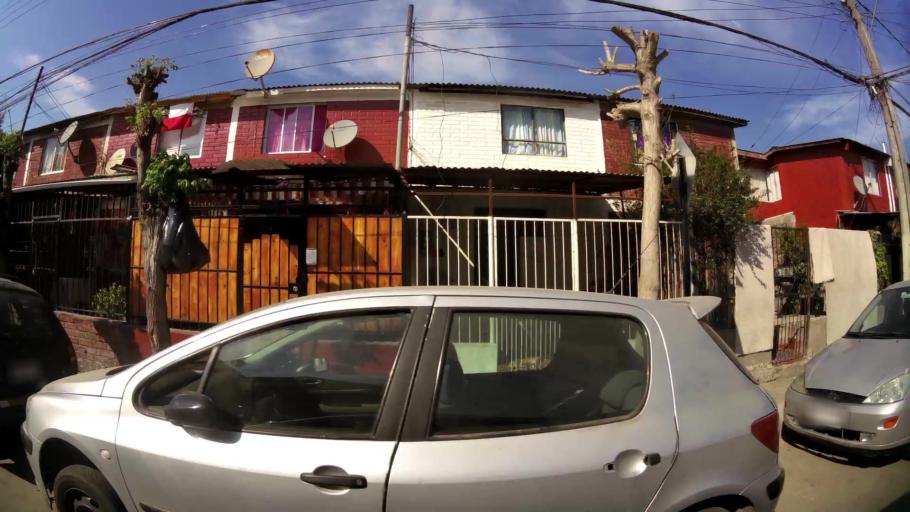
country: CL
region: Santiago Metropolitan
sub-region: Provincia de Santiago
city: Lo Prado
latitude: -33.4440
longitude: -70.7621
